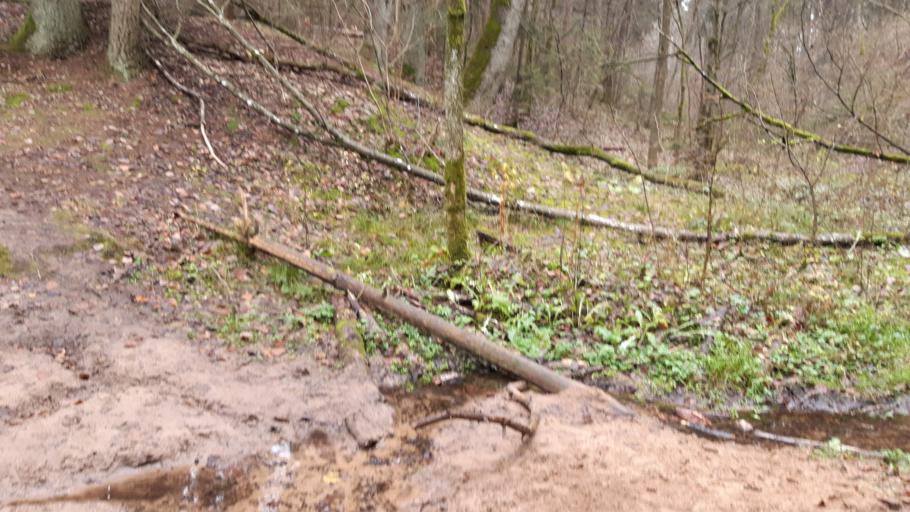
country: LT
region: Kauno apskritis
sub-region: Kaunas
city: Eiguliai
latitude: 54.9395
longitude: 23.9294
